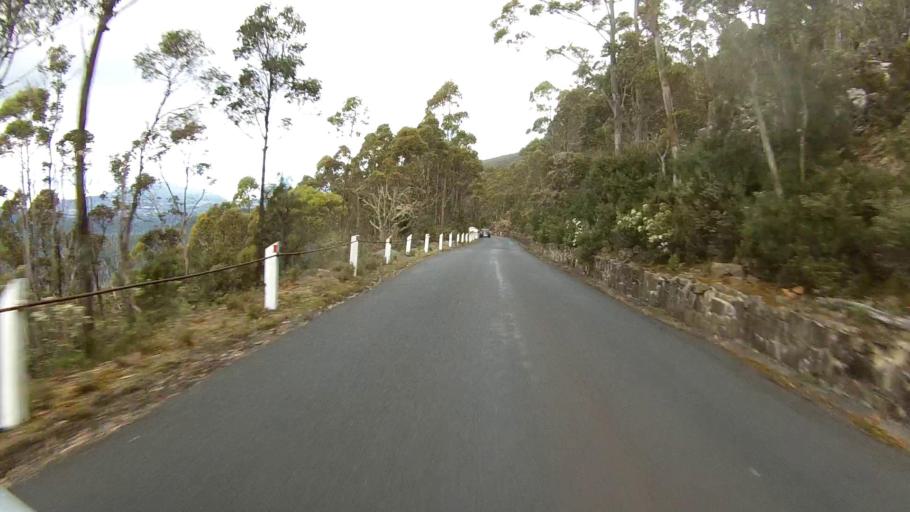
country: AU
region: Tasmania
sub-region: Glenorchy
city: West Moonah
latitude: -42.8968
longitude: 147.2443
